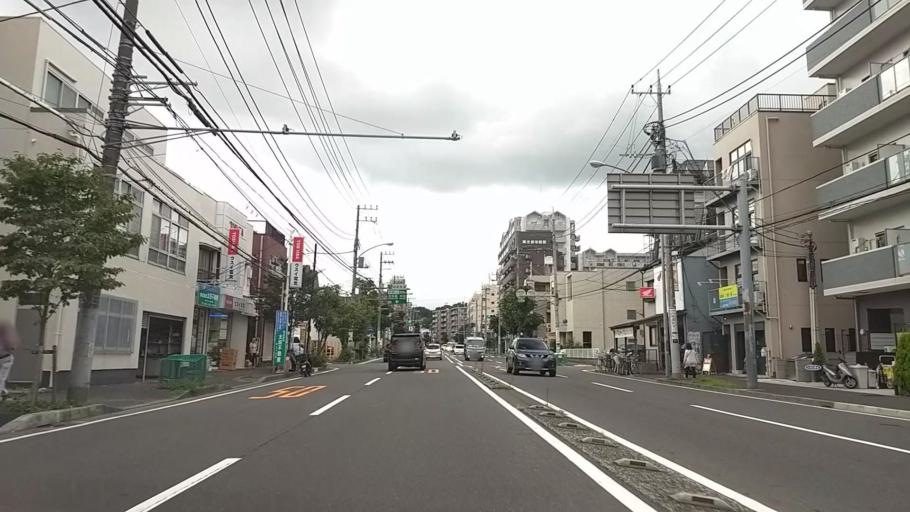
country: JP
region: Kanagawa
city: Yokohama
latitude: 35.4353
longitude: 139.6004
